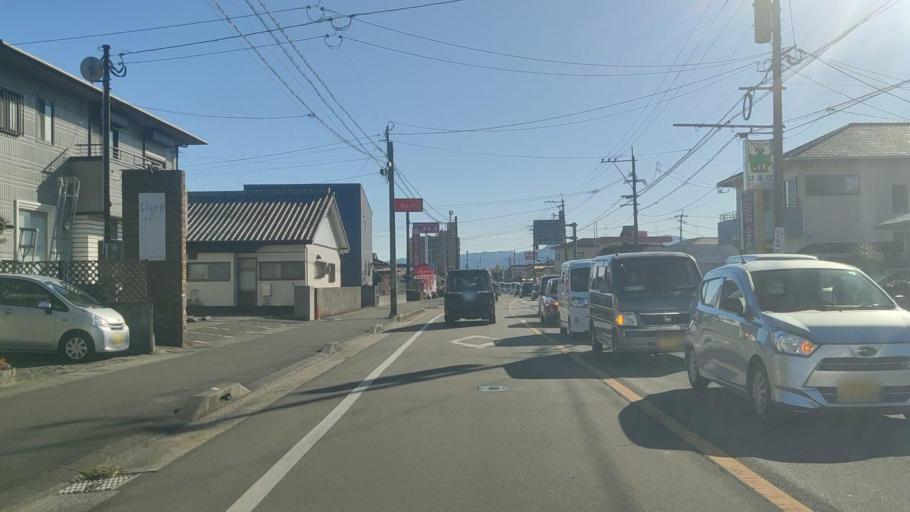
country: JP
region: Miyazaki
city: Miyazaki-shi
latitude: 31.8858
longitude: 131.4287
